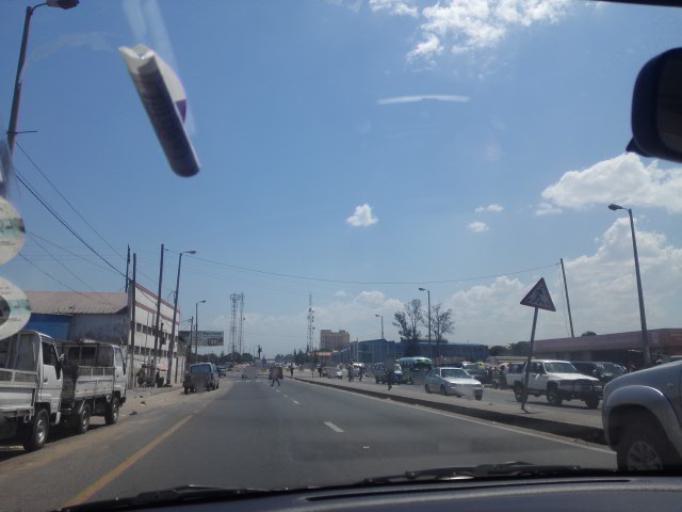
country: MZ
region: Maputo City
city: Maputo
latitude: -25.9335
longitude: 32.5515
